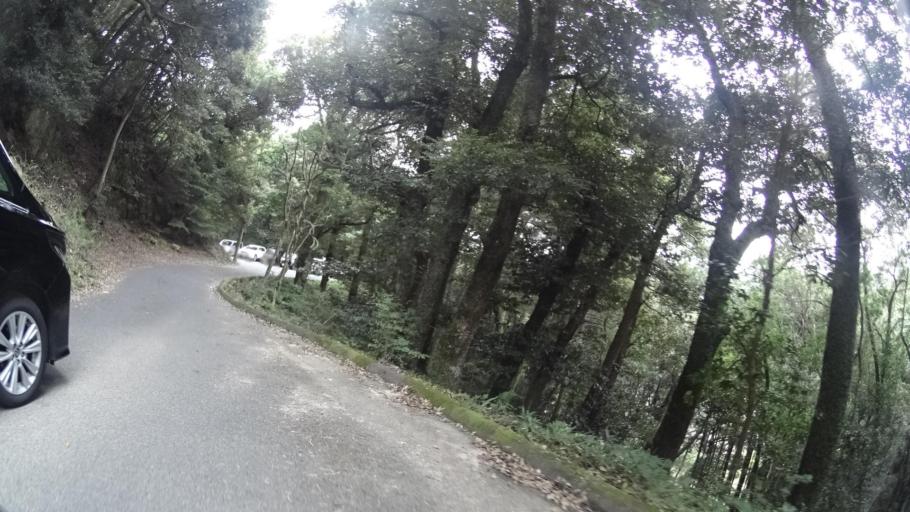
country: JP
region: Kyoto
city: Miyazu
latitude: 35.5287
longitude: 135.1840
